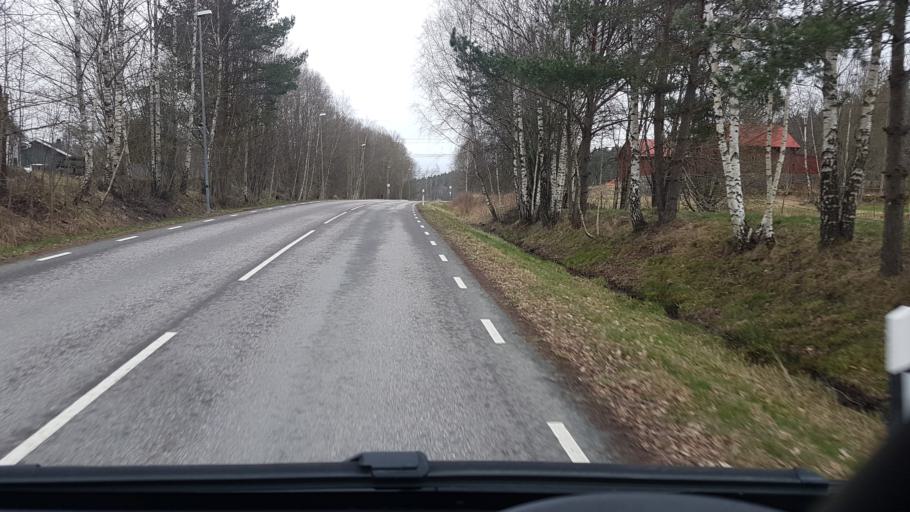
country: SE
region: Vaestra Goetaland
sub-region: Lerums Kommun
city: Stenkullen
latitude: 57.8020
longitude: 12.3345
